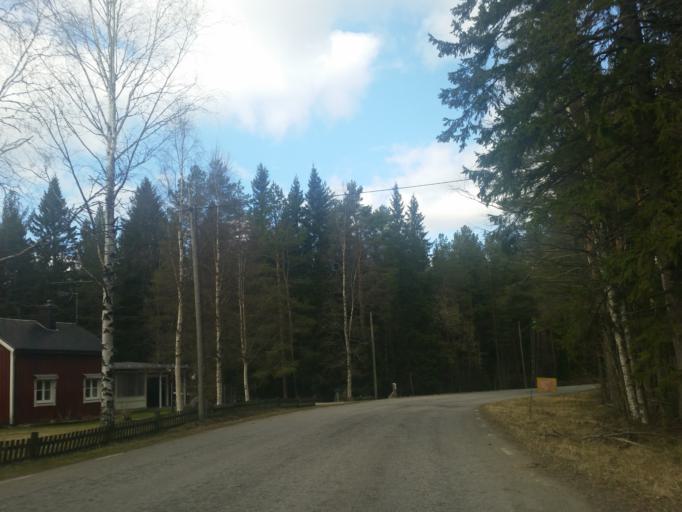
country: SE
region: Vaesterbotten
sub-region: Robertsfors Kommun
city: Robertsfors
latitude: 64.0494
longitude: 20.8502
